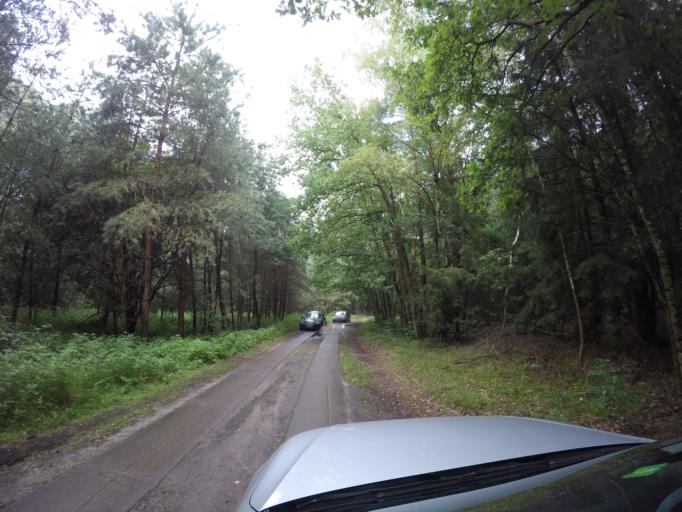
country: DE
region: Mecklenburg-Vorpommern
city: Wesenberg
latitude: 53.3801
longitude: 12.8953
